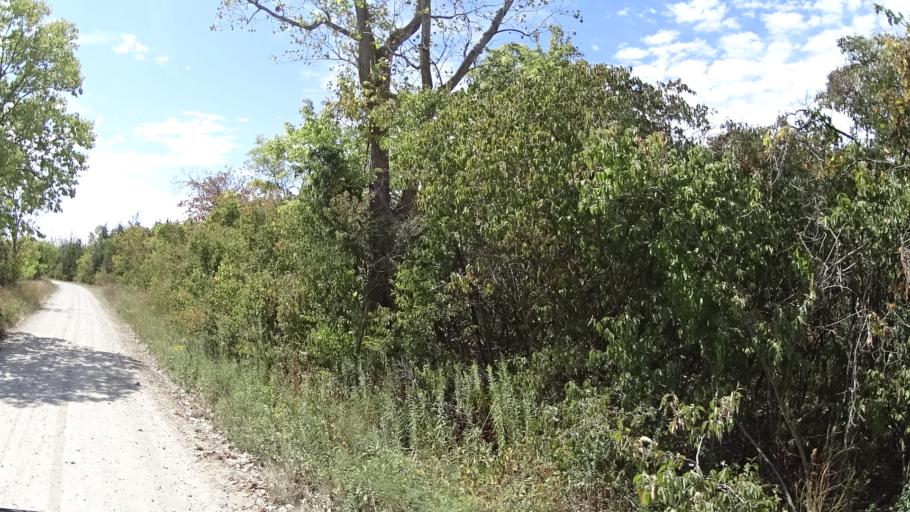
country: US
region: Ohio
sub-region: Erie County
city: Sandusky
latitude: 41.6043
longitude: -82.7197
